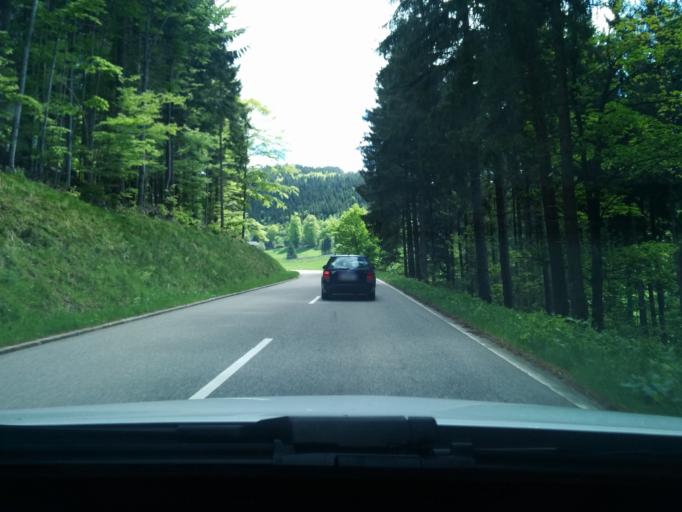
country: DE
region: Baden-Wuerttemberg
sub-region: Freiburg Region
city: Horben
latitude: 47.9158
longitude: 7.8765
